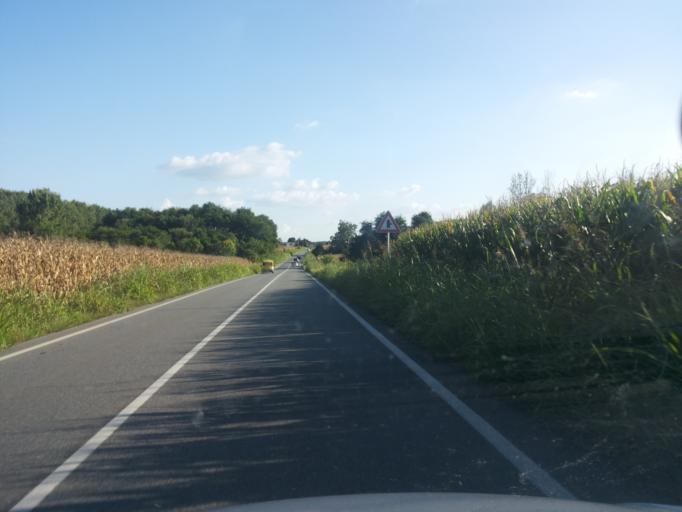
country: IT
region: Piedmont
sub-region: Provincia di Torino
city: Romano Canavese
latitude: 45.4035
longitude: 7.8831
